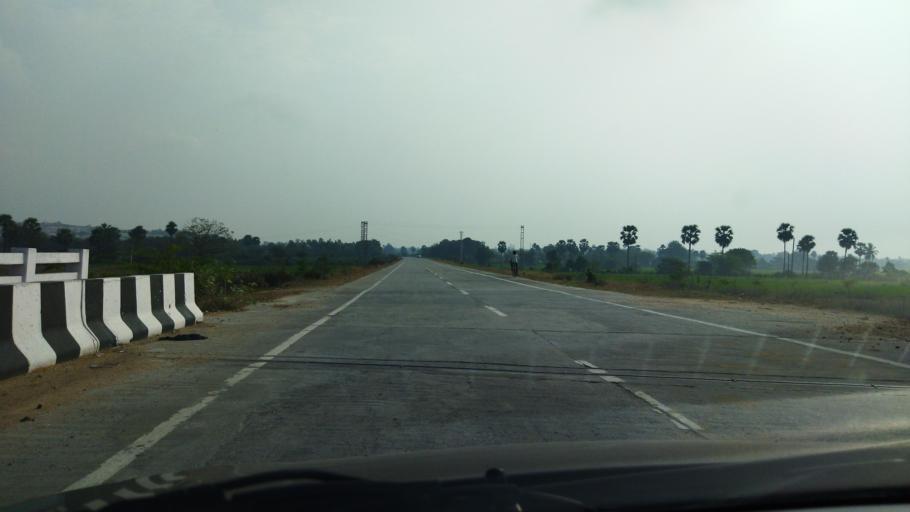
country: IN
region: Telangana
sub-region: Nalgonda
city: Nalgonda
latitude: 17.1779
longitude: 79.4035
